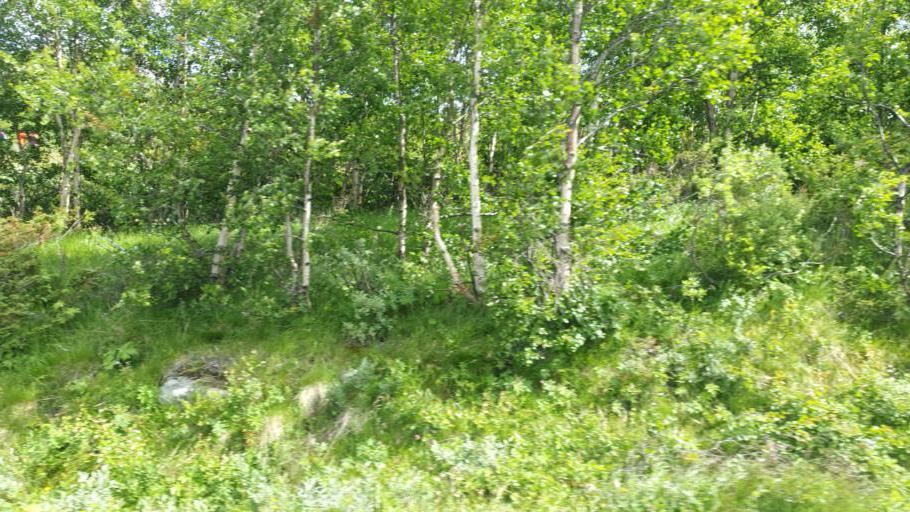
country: NO
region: Oppland
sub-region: Lom
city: Fossbergom
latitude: 61.4939
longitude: 8.8144
